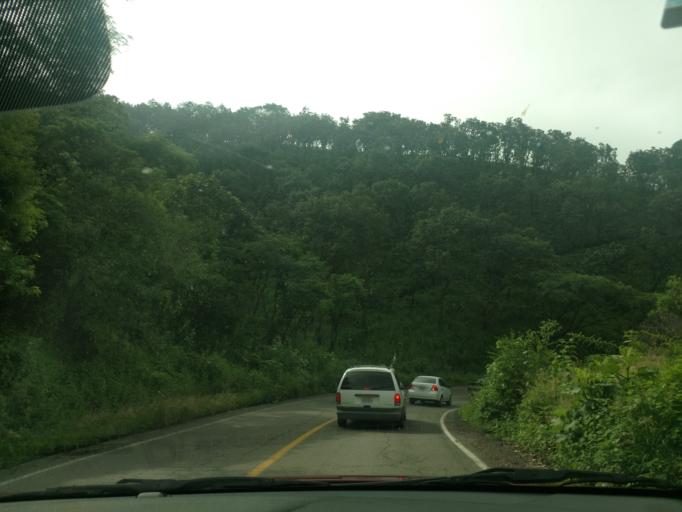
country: MX
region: Jalisco
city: El Salto
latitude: 20.4612
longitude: -104.3903
